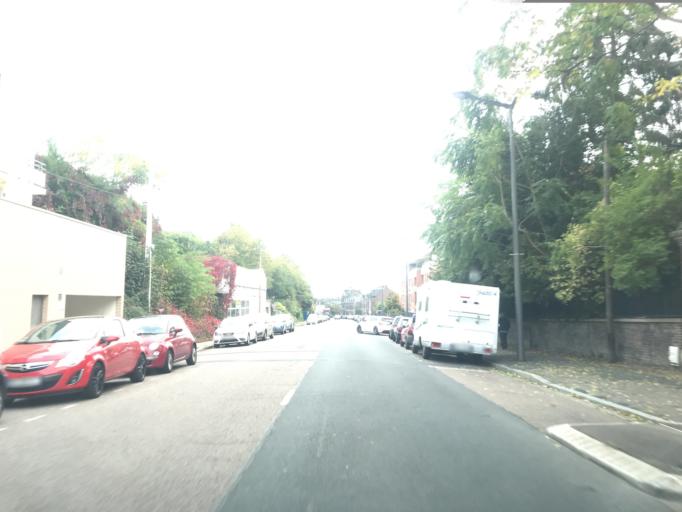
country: FR
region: Haute-Normandie
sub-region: Departement de la Seine-Maritime
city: Deville-les-Rouen
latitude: 49.4562
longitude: 1.0559
